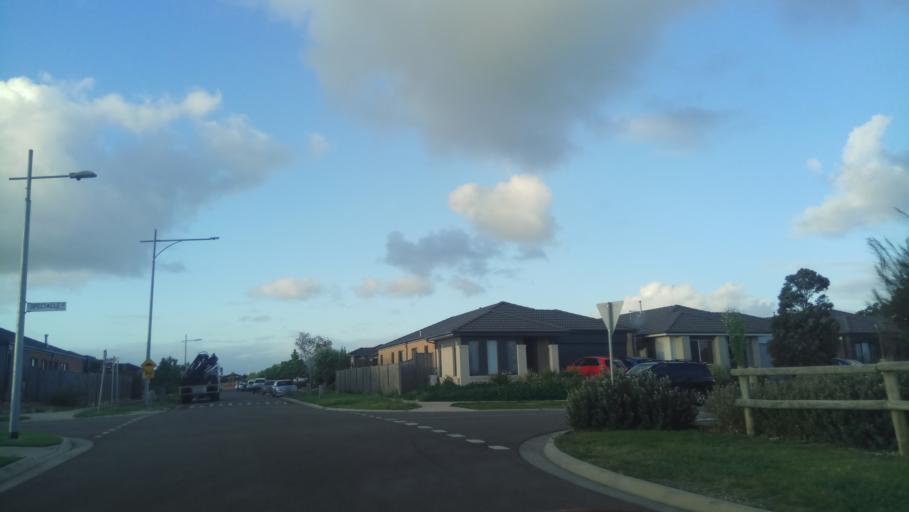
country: AU
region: Victoria
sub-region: Wyndham
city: Point Cook
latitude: -37.9143
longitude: 144.7701
